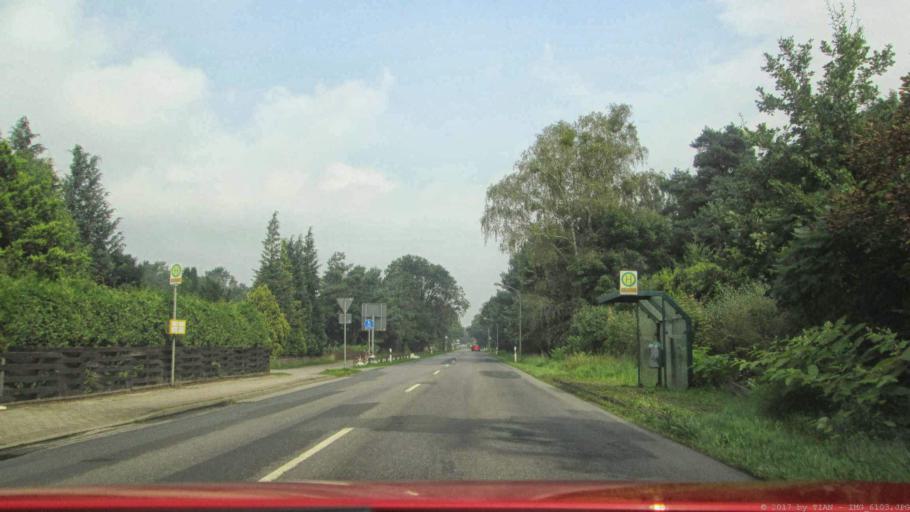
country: DE
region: Lower Saxony
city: Wagenhoff
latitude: 52.5564
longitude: 10.5131
